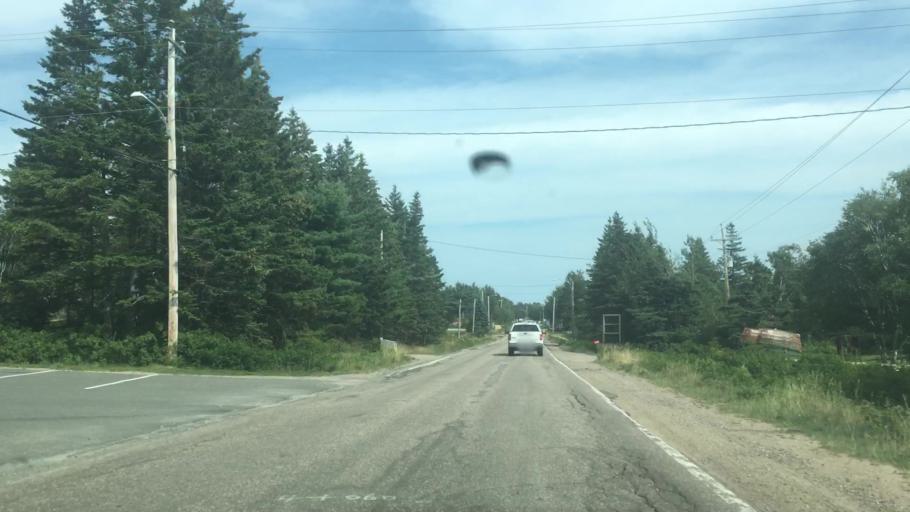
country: CA
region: Nova Scotia
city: Sydney Mines
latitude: 46.6897
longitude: -60.3887
